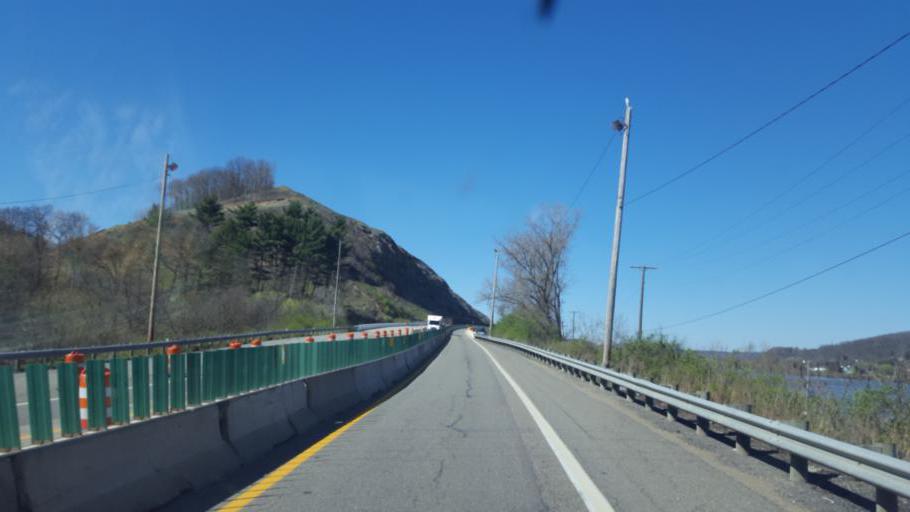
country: US
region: West Virginia
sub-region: Brooke County
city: Wellsburg
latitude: 40.2717
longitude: -80.6186
